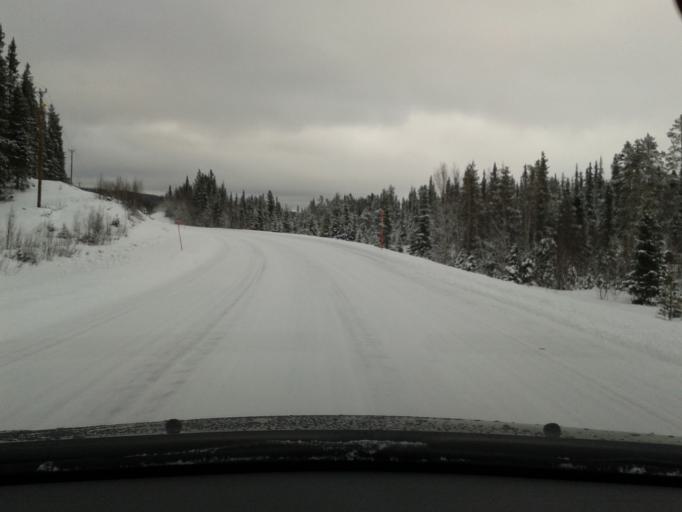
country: SE
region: Vaesterbotten
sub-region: Vilhelmina Kommun
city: Sjoberg
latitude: 65.2375
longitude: 15.7914
